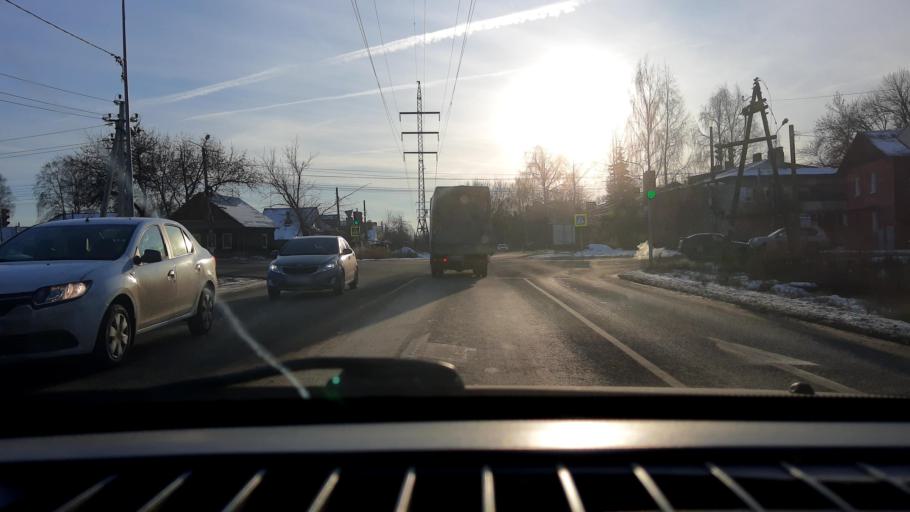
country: RU
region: Nizjnij Novgorod
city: Bor
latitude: 56.3647
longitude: 44.0721
